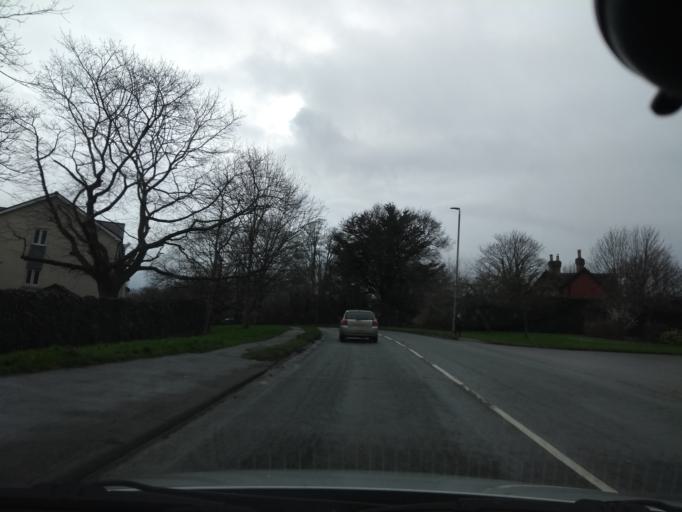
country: GB
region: England
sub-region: Somerset
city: Taunton
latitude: 51.0293
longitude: -3.1397
